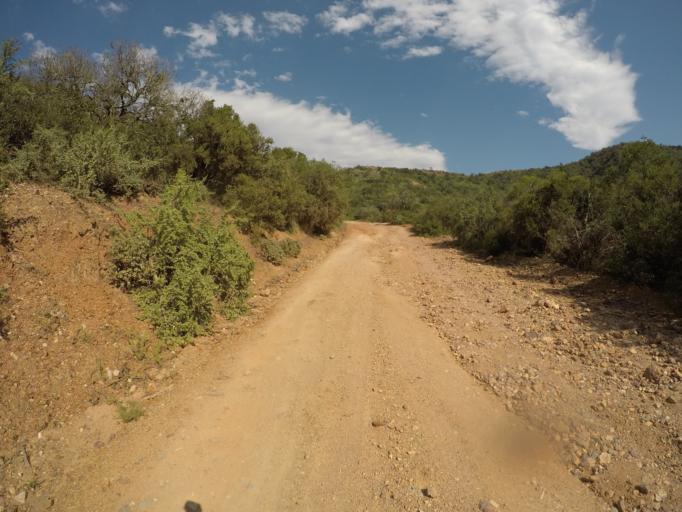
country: ZA
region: Eastern Cape
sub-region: Cacadu District Municipality
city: Kareedouw
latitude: -33.6567
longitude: 24.4280
